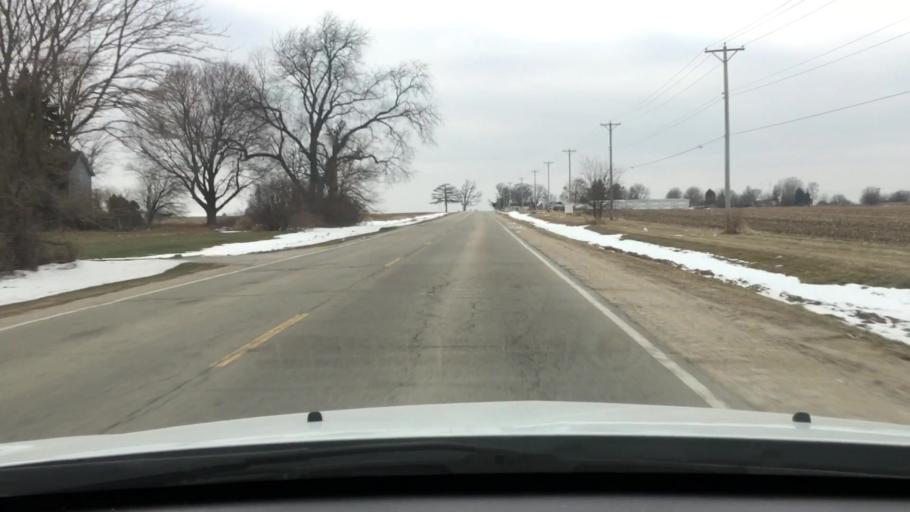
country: US
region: Illinois
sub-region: Ogle County
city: Rochelle
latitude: 41.8979
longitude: -89.0471
